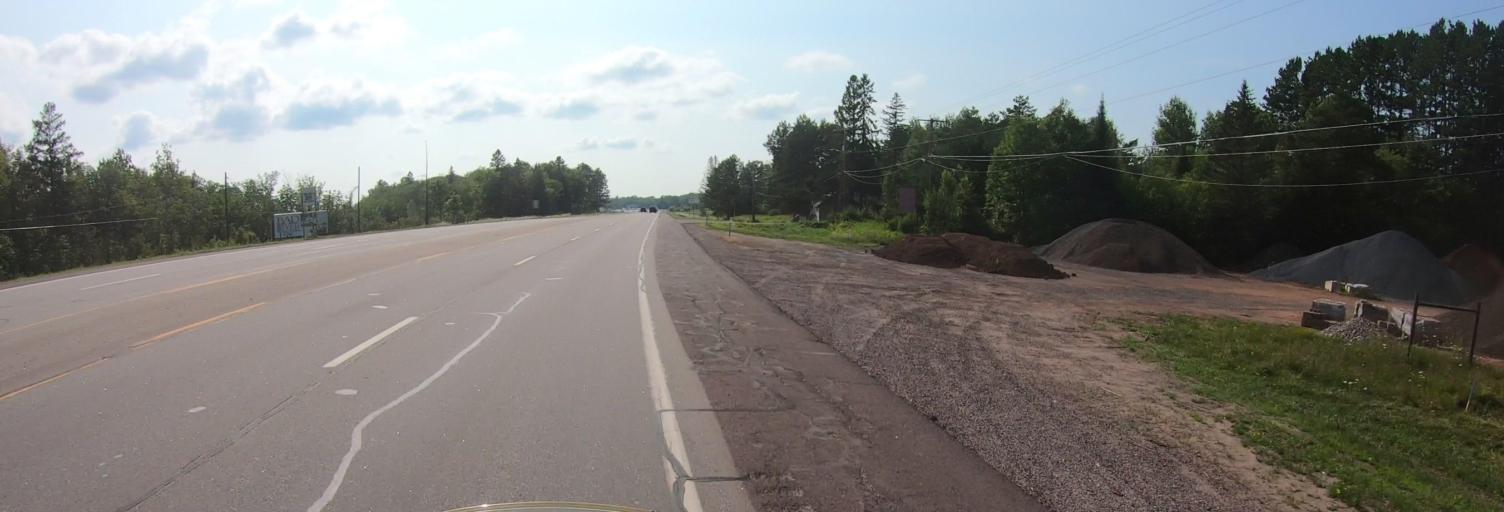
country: US
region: Michigan
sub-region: Gogebic County
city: Bessemer
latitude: 46.4781
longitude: -90.0929
